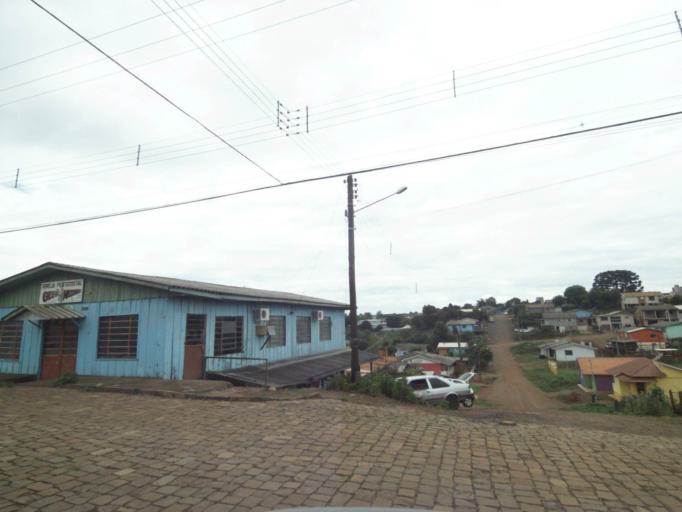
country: BR
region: Rio Grande do Sul
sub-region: Lagoa Vermelha
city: Lagoa Vermelha
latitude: -28.2178
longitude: -51.5370
